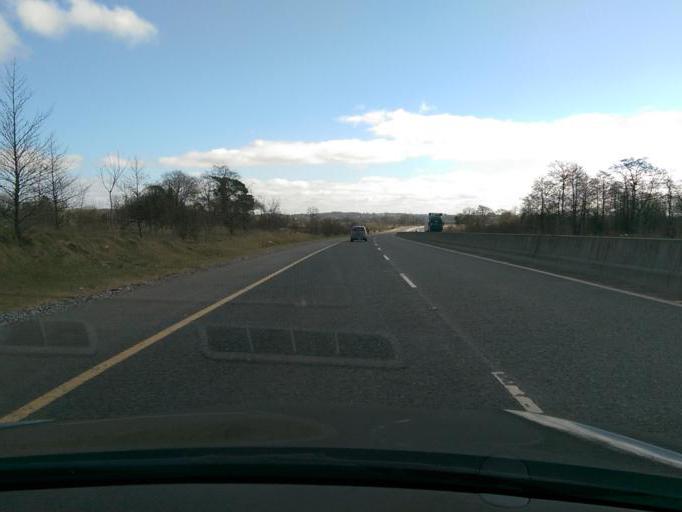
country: IE
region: Leinster
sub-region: Uibh Fhaili
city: Clara
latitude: 53.3937
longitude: -7.6296
